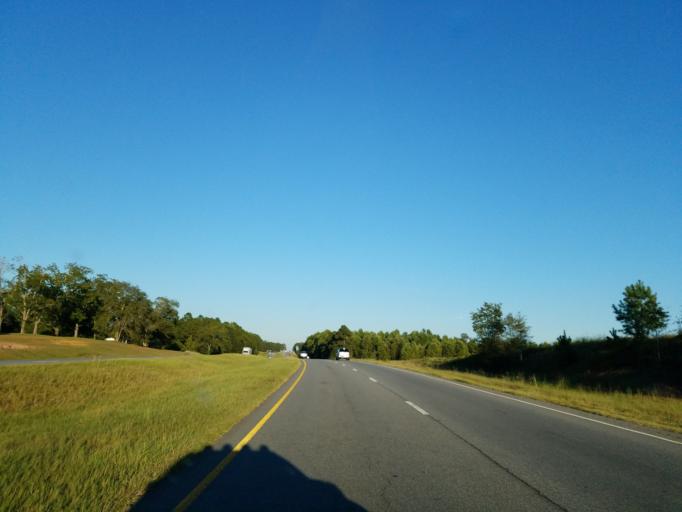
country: US
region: Georgia
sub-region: Worth County
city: Sylvester
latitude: 31.5099
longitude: -83.7689
